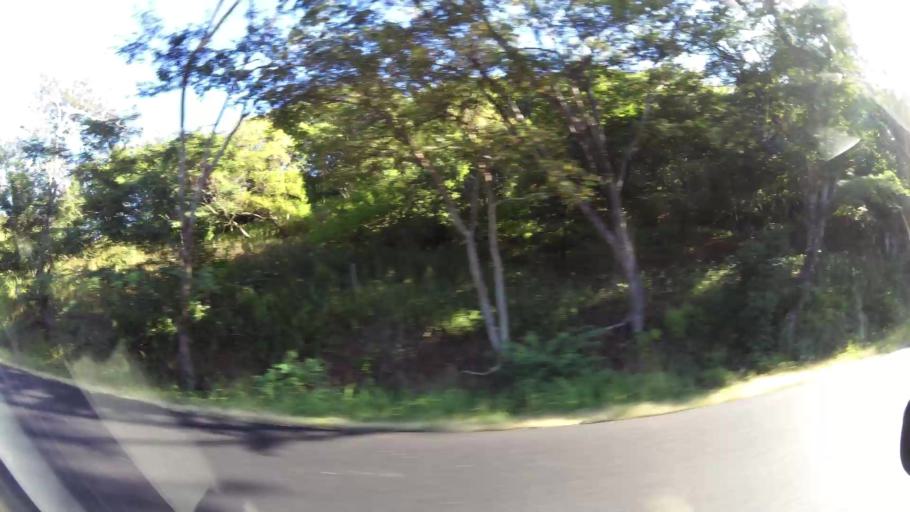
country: CR
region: Guanacaste
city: Sardinal
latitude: 10.5294
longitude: -85.6587
